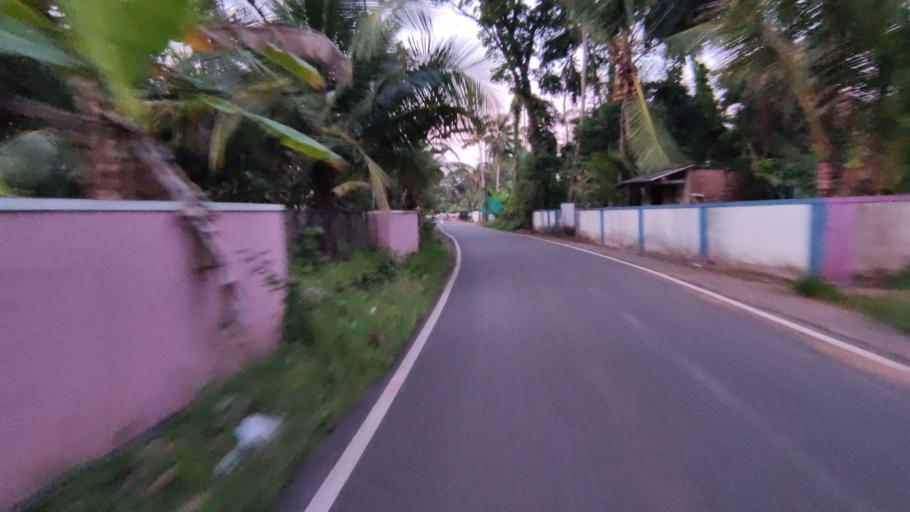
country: IN
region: Kerala
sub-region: Kottayam
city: Kottayam
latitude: 9.5807
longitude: 76.4354
